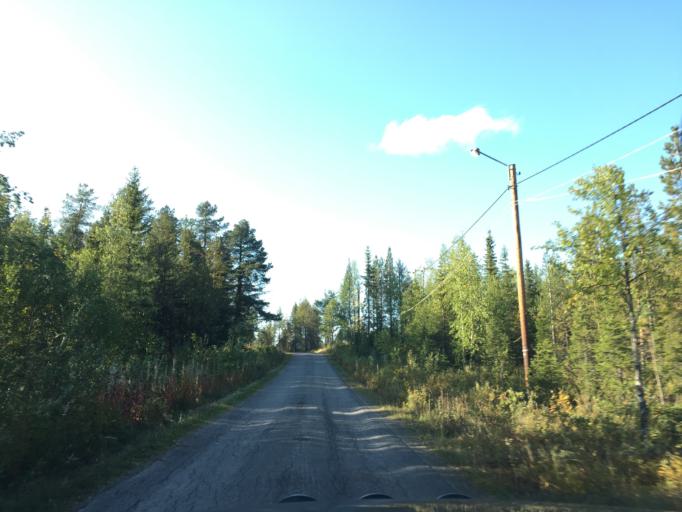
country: SE
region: Norrbotten
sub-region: Gallivare Kommun
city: Malmberget
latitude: 67.6534
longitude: 21.0393
